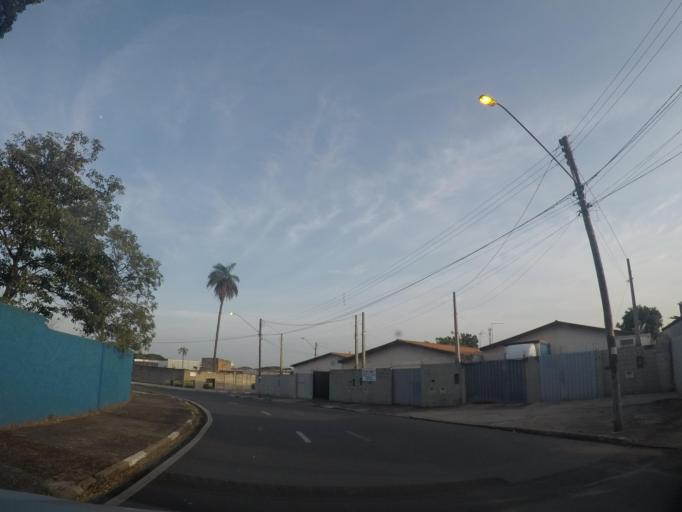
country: BR
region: Sao Paulo
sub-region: Hortolandia
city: Hortolandia
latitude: -22.8529
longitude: -47.1607
